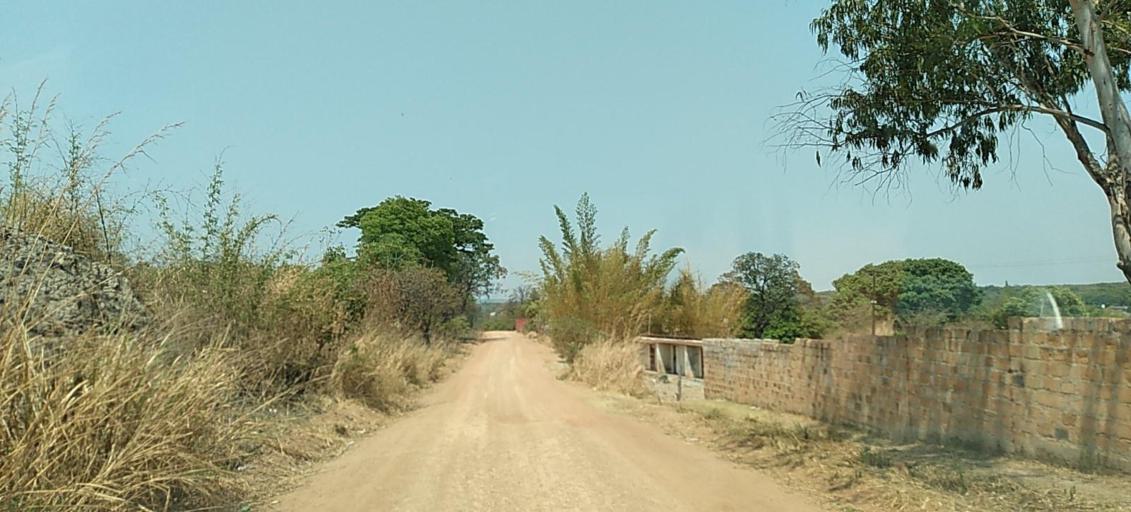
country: ZM
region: Copperbelt
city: Chambishi
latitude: -12.6056
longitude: 27.9618
